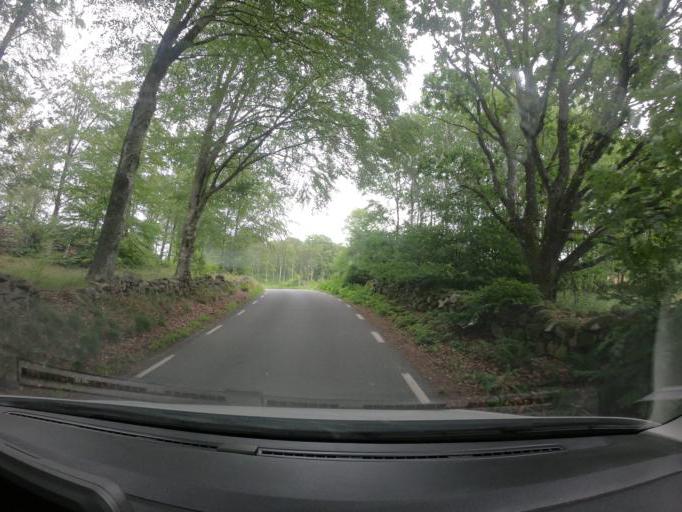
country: SE
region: Skane
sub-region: Hoors Kommun
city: Hoeoer
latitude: 56.0097
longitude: 13.5381
